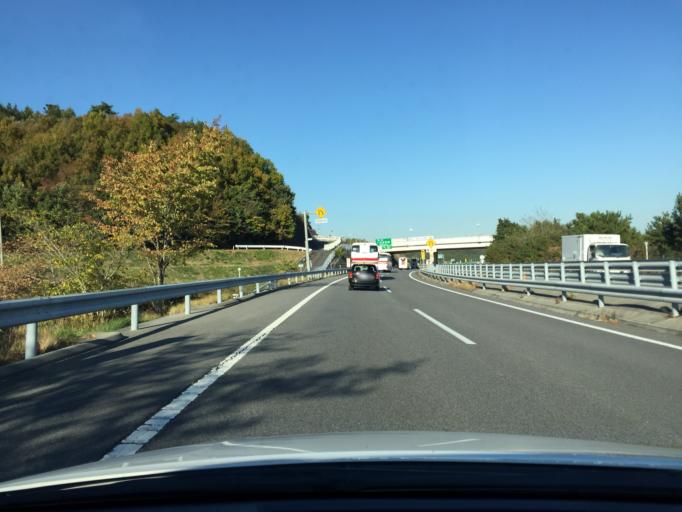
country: JP
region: Fukushima
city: Iwaki
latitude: 37.0629
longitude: 140.8330
